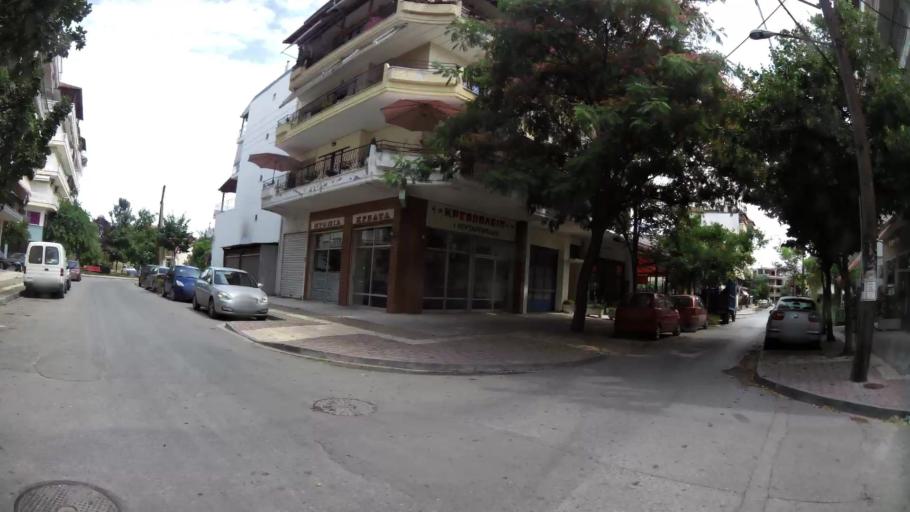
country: GR
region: Central Macedonia
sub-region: Nomos Pierias
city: Katerini
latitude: 40.2745
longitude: 22.5104
